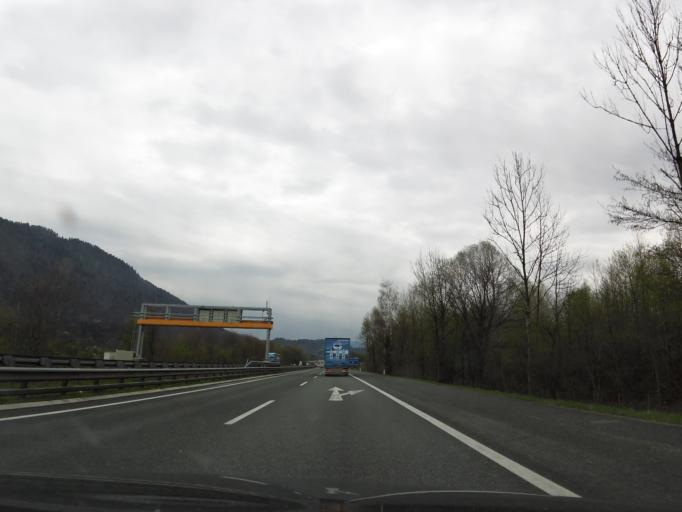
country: AT
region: Tyrol
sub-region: Politischer Bezirk Kufstein
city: Schwoich
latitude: 47.5633
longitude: 12.1380
